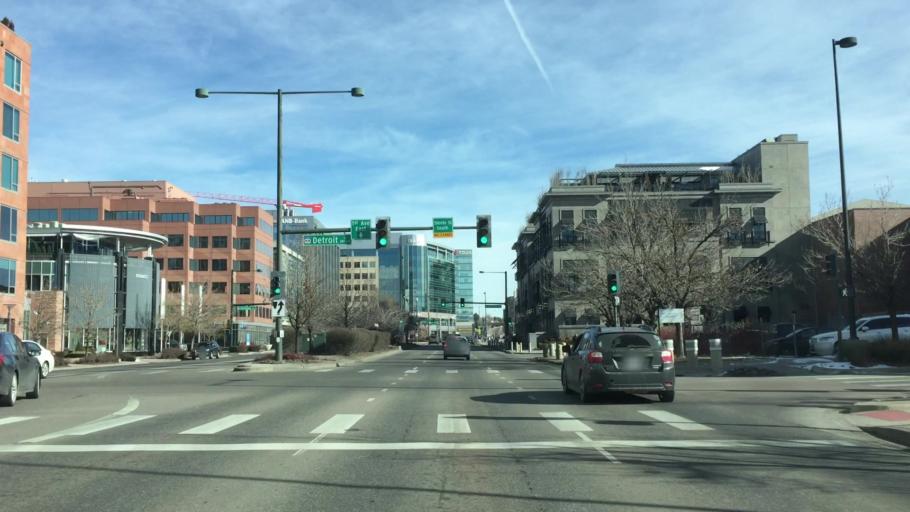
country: US
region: Colorado
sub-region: Arapahoe County
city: Glendale
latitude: 39.7180
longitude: -104.9549
